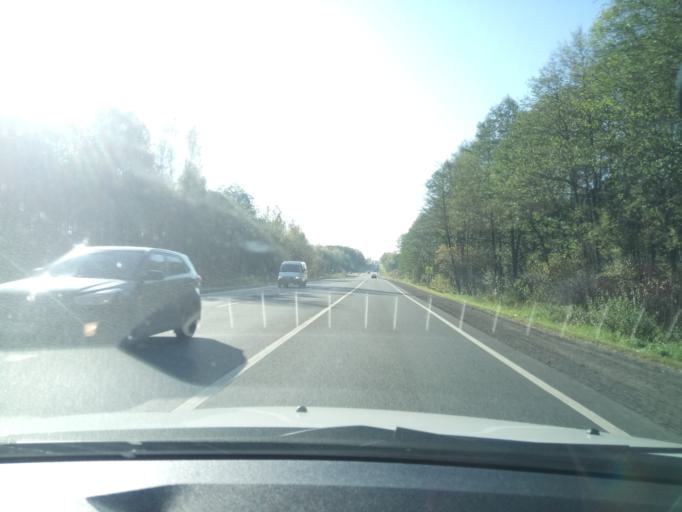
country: RU
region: Nizjnij Novgorod
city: Dal'neye Konstantinovo
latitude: 55.9842
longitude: 43.9709
